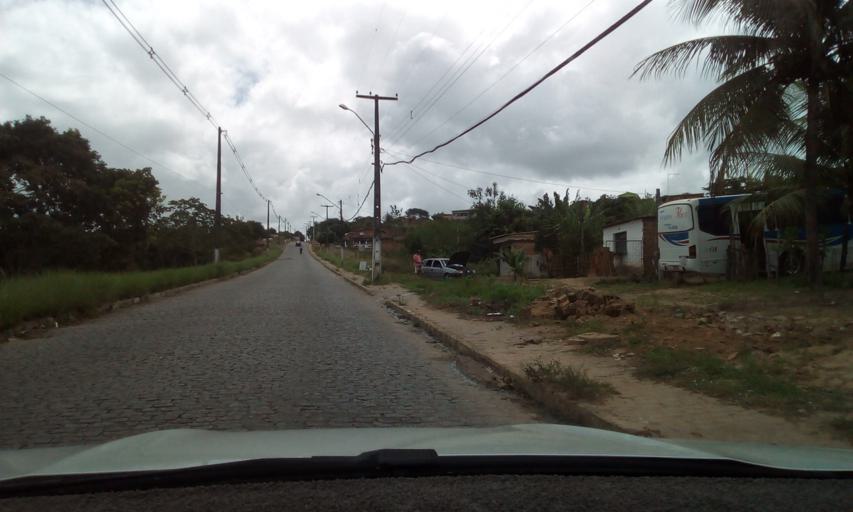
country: BR
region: Paraiba
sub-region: Rio Tinto
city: Rio Tinto
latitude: -6.7976
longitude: -35.0703
